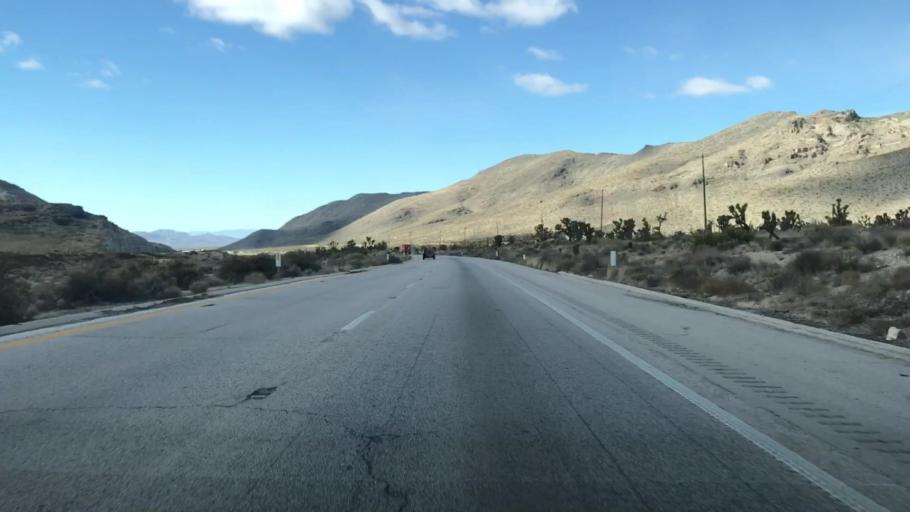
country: US
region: Nevada
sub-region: Clark County
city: Sandy Valley
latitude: 35.4746
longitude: -115.5670
